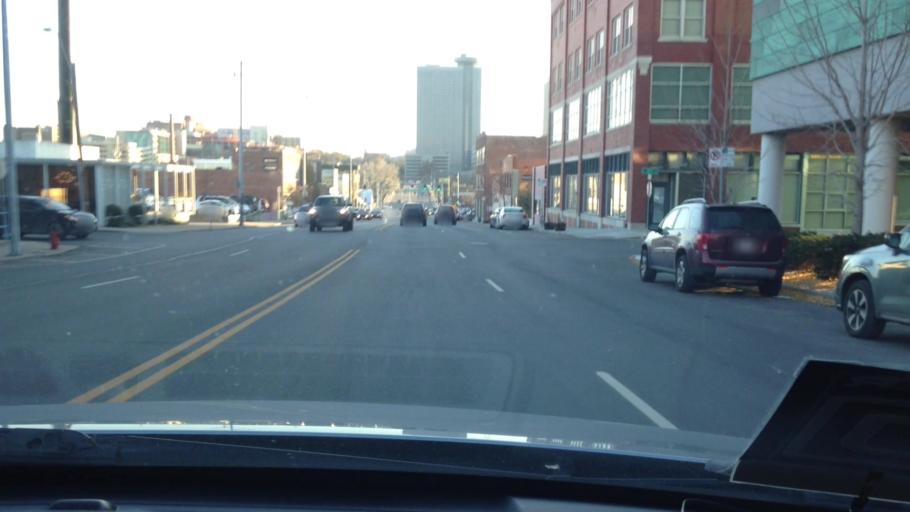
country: US
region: Missouri
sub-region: Jackson County
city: Kansas City
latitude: 39.0936
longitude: -94.5789
